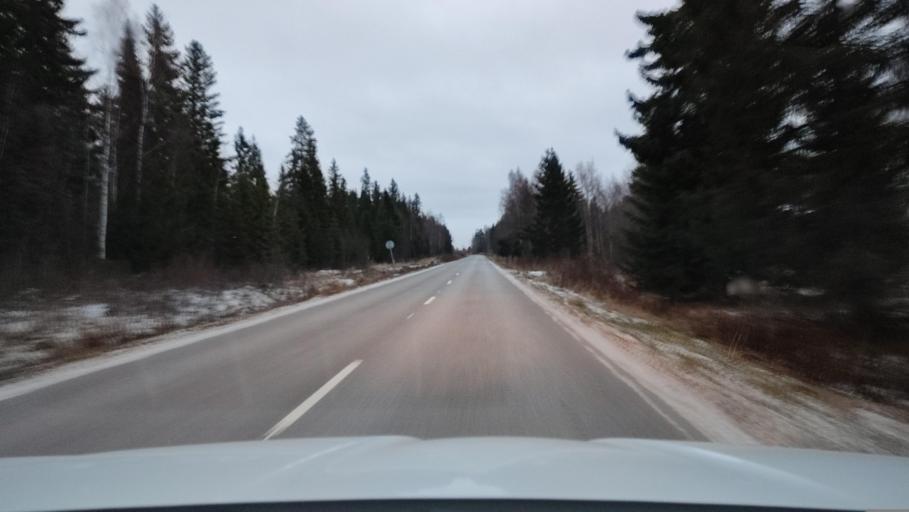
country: FI
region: Ostrobothnia
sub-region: Vaasa
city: Replot
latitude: 63.2371
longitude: 21.3940
